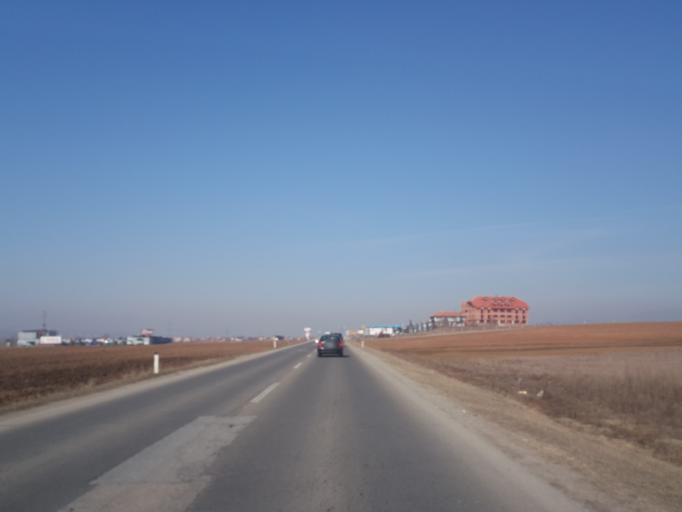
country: XK
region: Mitrovica
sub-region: Vushtrri
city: Vushtrri
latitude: 42.7719
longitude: 21.0195
